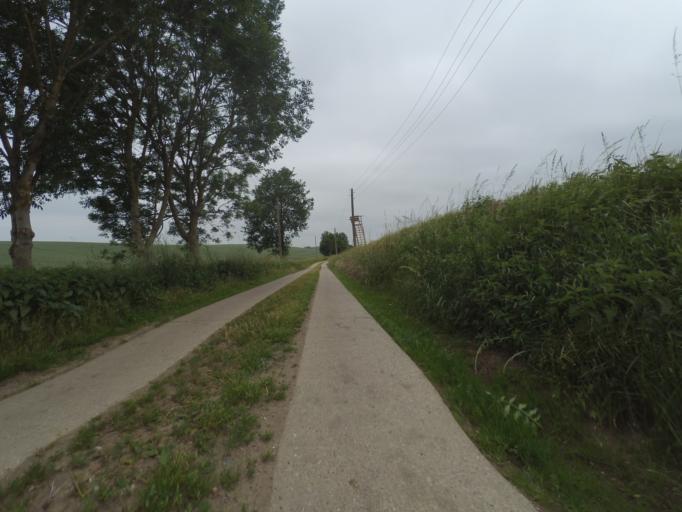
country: DE
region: Mecklenburg-Vorpommern
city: Dabel
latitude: 53.6732
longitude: 11.9240
